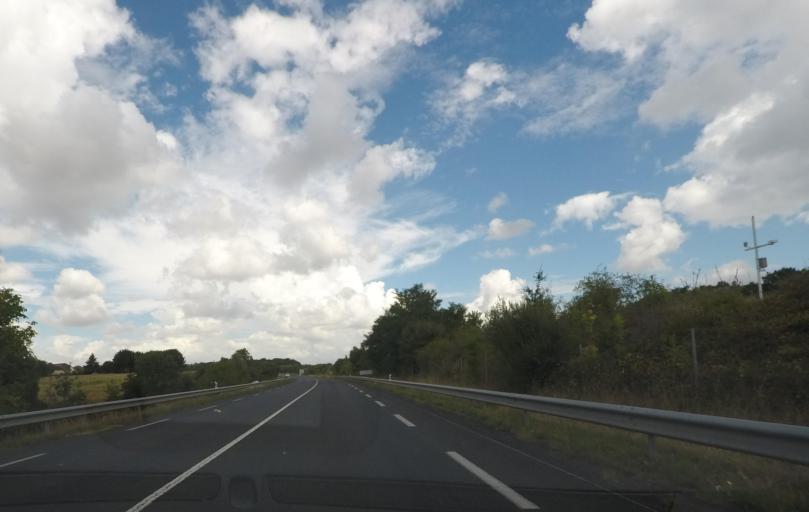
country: FR
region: Pays de la Loire
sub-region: Departement de la Sarthe
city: Champagne
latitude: 48.0391
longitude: 0.2939
